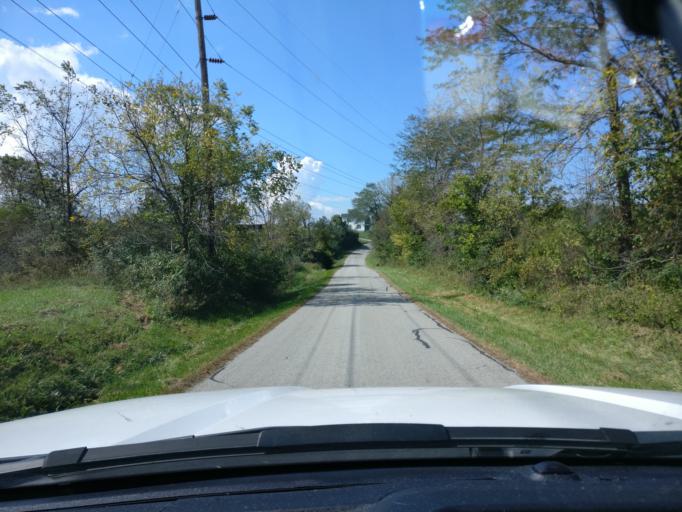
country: US
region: Ohio
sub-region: Clinton County
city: Wilmington
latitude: 39.4624
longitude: -83.9540
